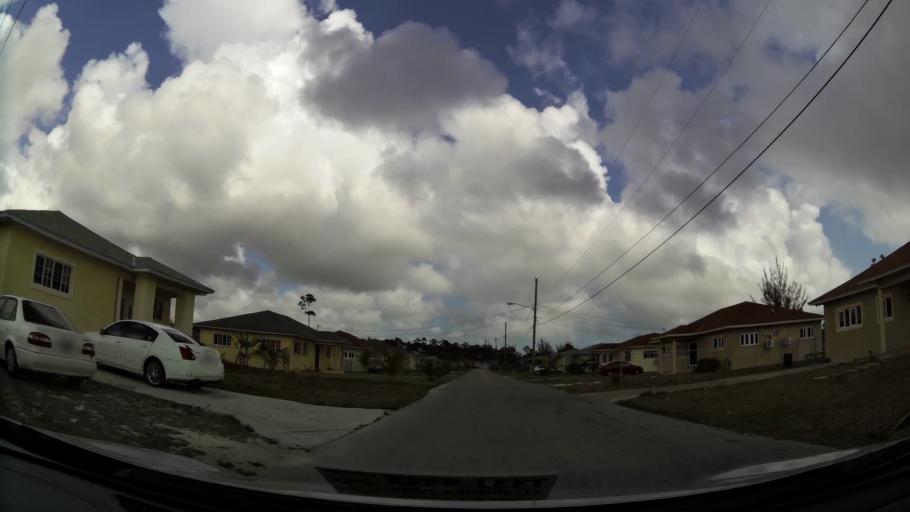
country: BS
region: Freeport
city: Freeport
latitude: 26.5203
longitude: -78.7267
